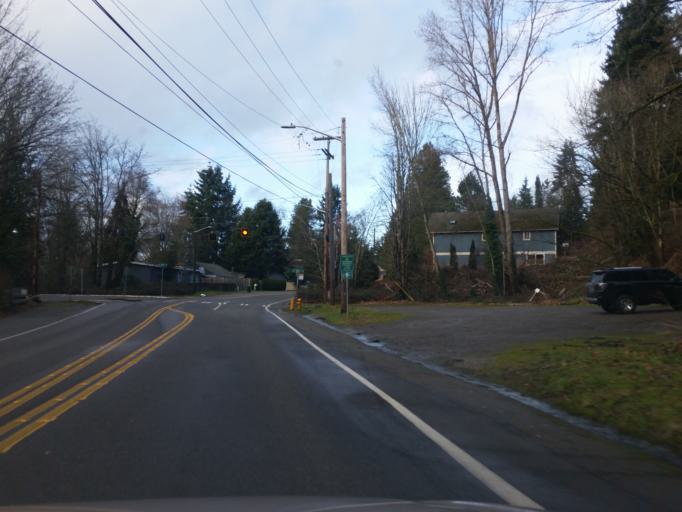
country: US
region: Washington
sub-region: King County
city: Inglewood-Finn Hill
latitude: 47.6968
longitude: -122.2772
